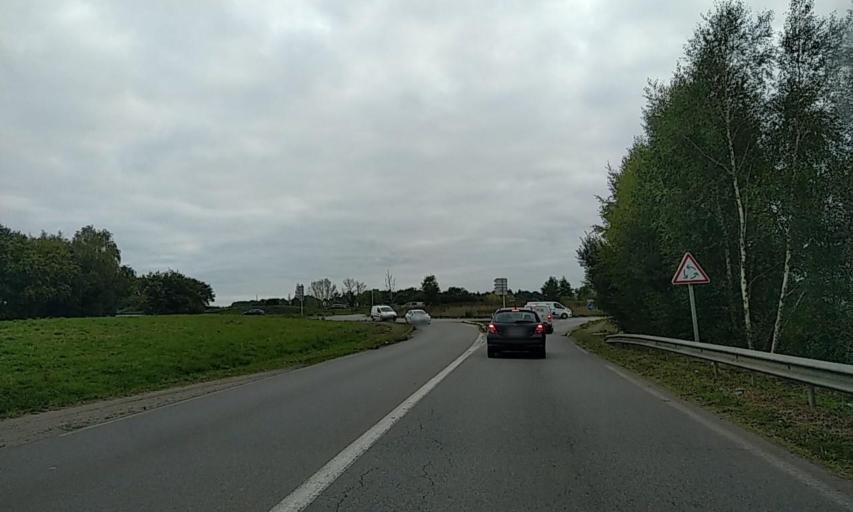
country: FR
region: Brittany
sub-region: Departement du Morbihan
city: Lanester
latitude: 47.7824
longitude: -3.3439
